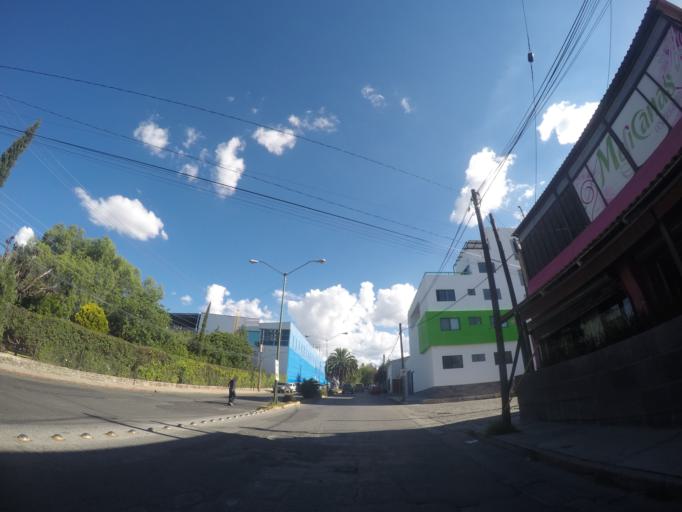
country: MX
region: San Luis Potosi
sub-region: San Luis Potosi
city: San Luis Potosi
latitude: 22.1507
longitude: -101.0196
